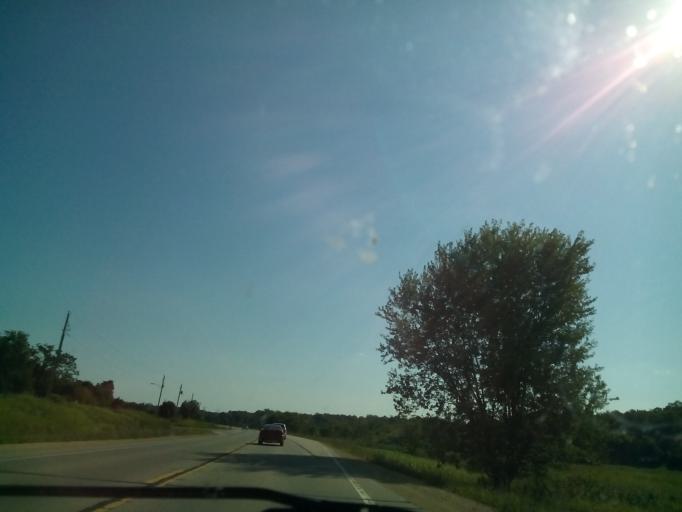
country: US
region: Wisconsin
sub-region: Green County
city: New Glarus
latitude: 42.8456
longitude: -89.6315
